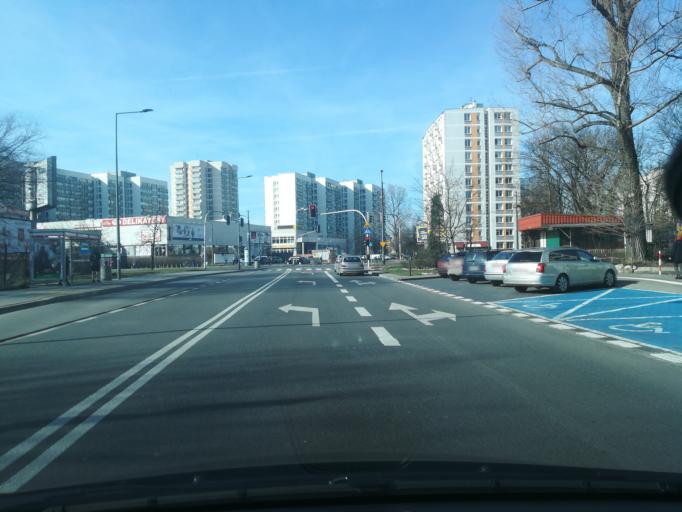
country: PL
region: Masovian Voivodeship
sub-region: Warszawa
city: Praga Poludnie
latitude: 52.2416
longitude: 21.0721
